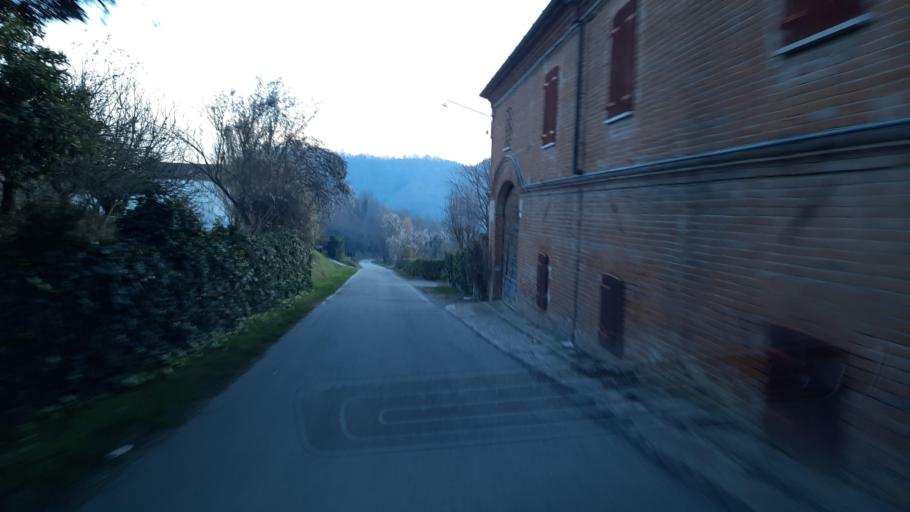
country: IT
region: Piedmont
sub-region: Provincia di Alessandria
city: Camino
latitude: 45.1570
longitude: 8.2737
